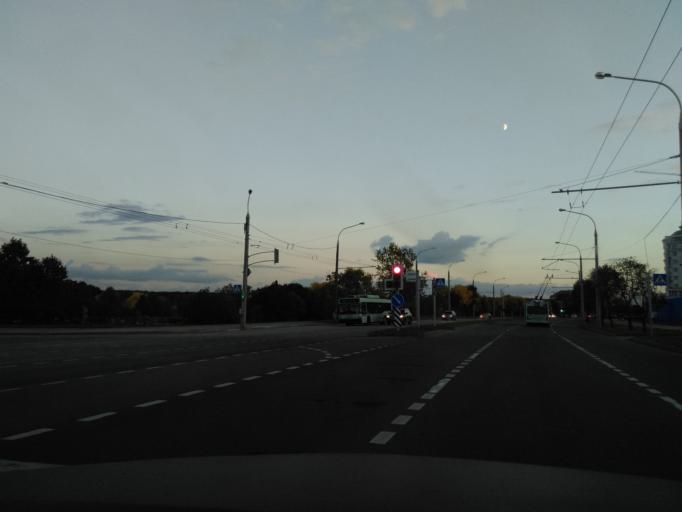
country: BY
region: Minsk
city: Minsk
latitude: 53.9284
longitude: 27.6395
